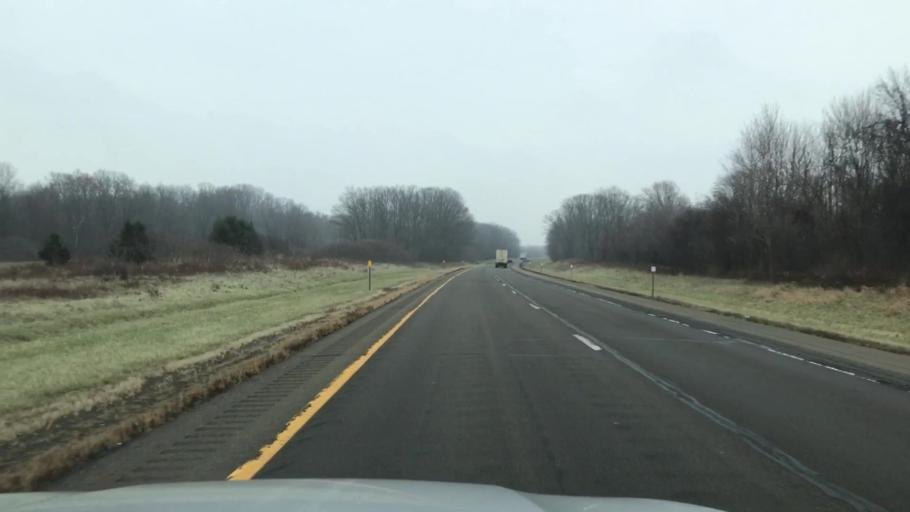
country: US
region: New York
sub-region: Chautauqua County
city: Westfield
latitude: 42.2866
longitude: -79.6867
